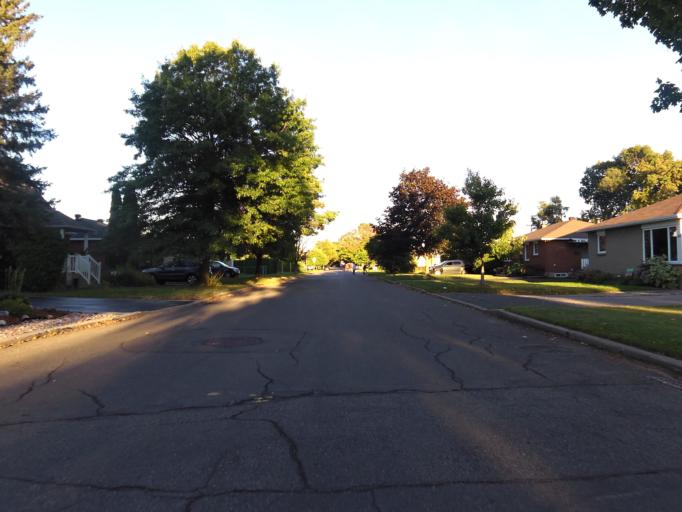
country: CA
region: Ontario
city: Ottawa
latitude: 45.4287
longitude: -75.6541
